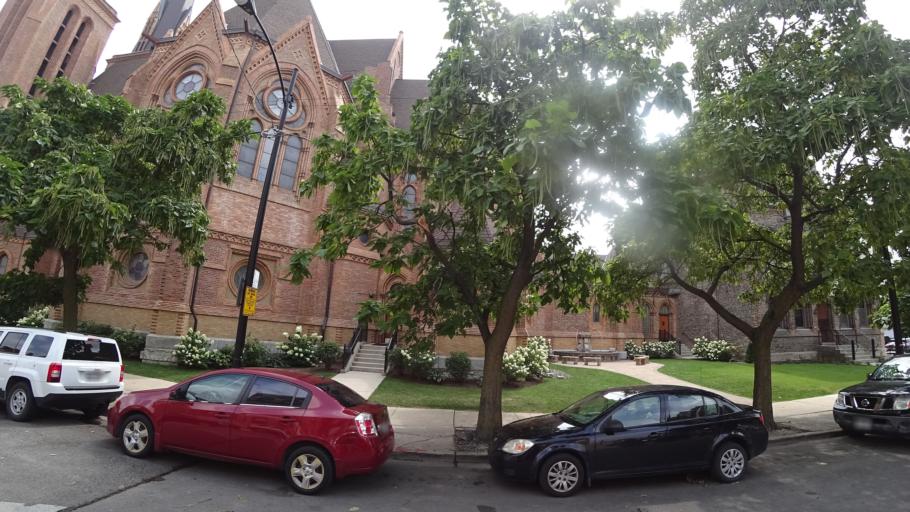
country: US
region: Illinois
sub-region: Cook County
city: Chicago
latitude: 41.8512
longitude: -87.6791
